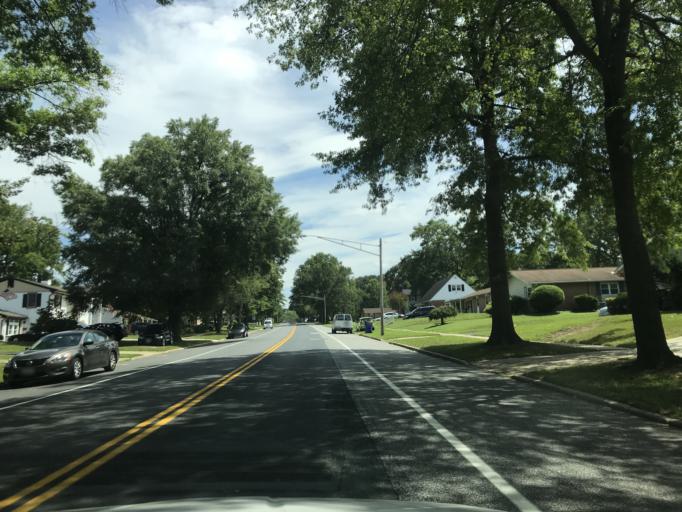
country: US
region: Maryland
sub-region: Harford County
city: Joppatowne
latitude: 39.4174
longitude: -76.3650
